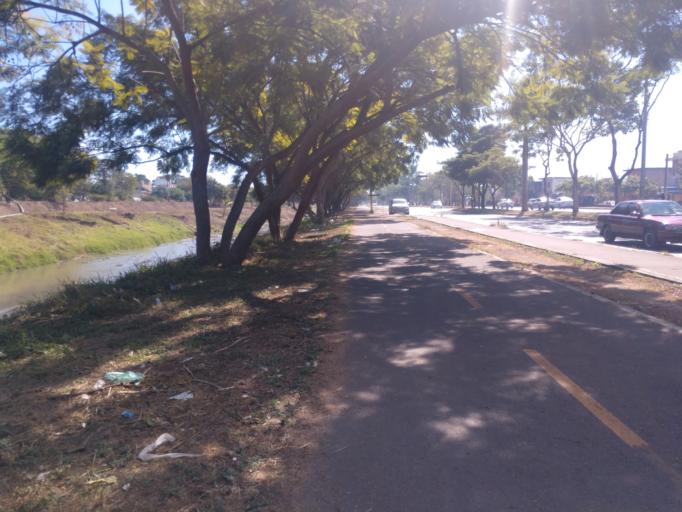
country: MX
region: Nayarit
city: Tepic
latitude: 21.5074
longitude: -104.8763
